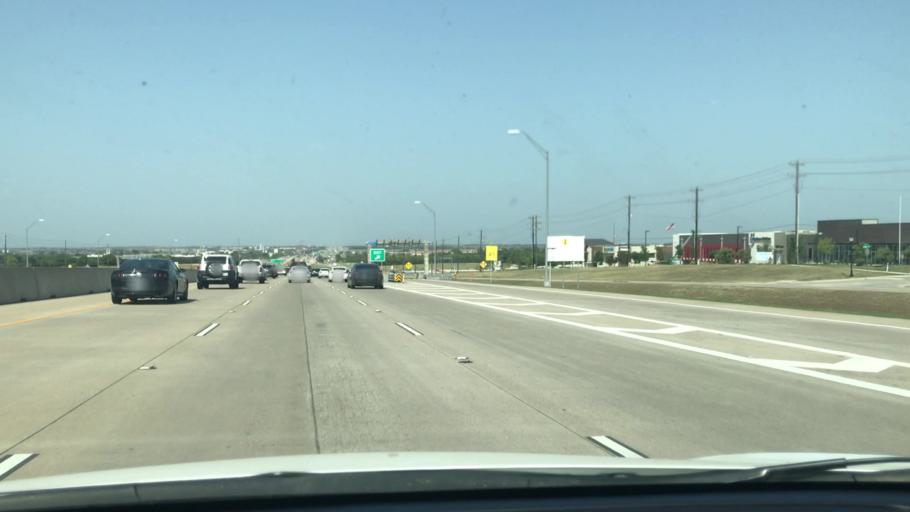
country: US
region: Texas
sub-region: Collin County
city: Frisco
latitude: 33.1131
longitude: -96.7656
